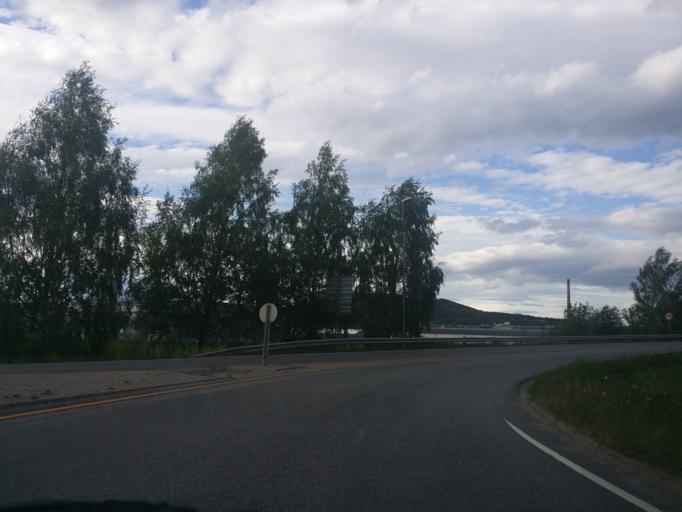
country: NO
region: Hedmark
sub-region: Ringsaker
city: Brumunddal
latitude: 60.8800
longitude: 10.9305
